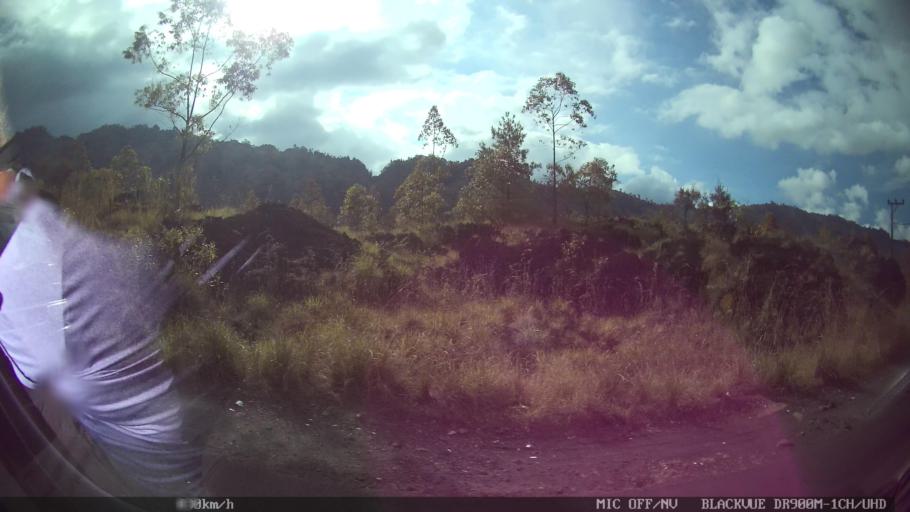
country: ID
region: Bali
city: Banjar Kedisan
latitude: -8.2383
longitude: 115.3531
